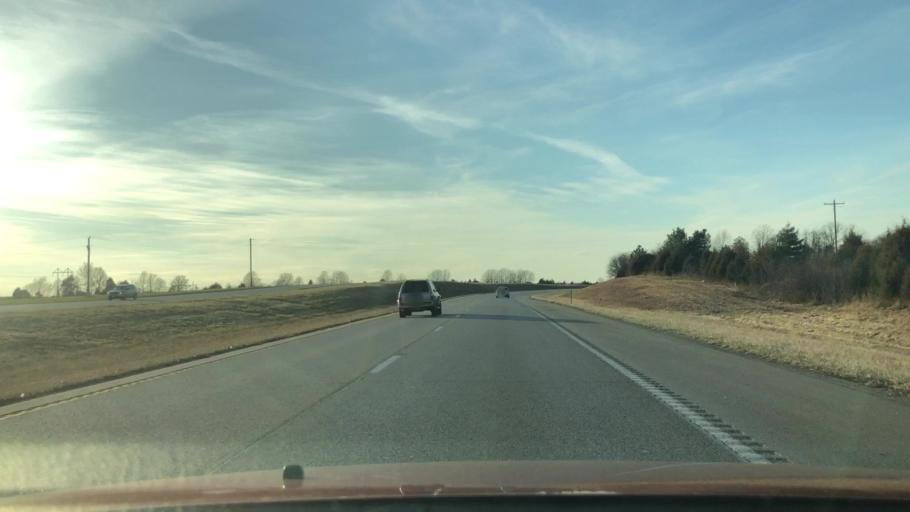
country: US
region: Missouri
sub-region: Webster County
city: Seymour
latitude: 37.1187
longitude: -92.6889
